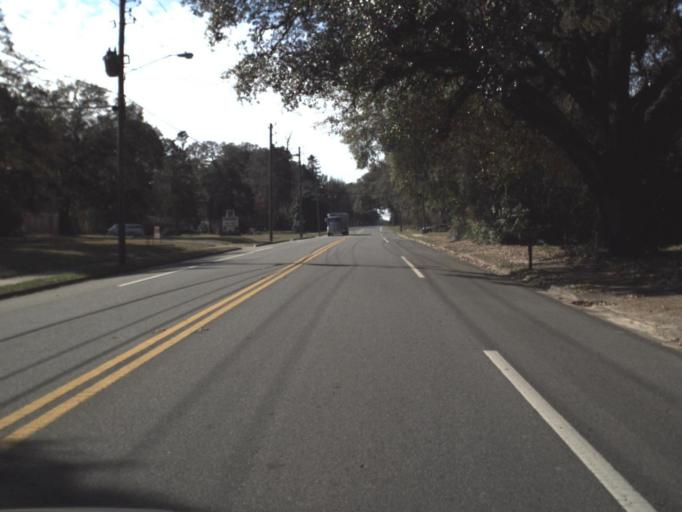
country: US
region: Florida
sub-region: Jackson County
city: Malone
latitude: 30.8682
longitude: -85.1625
